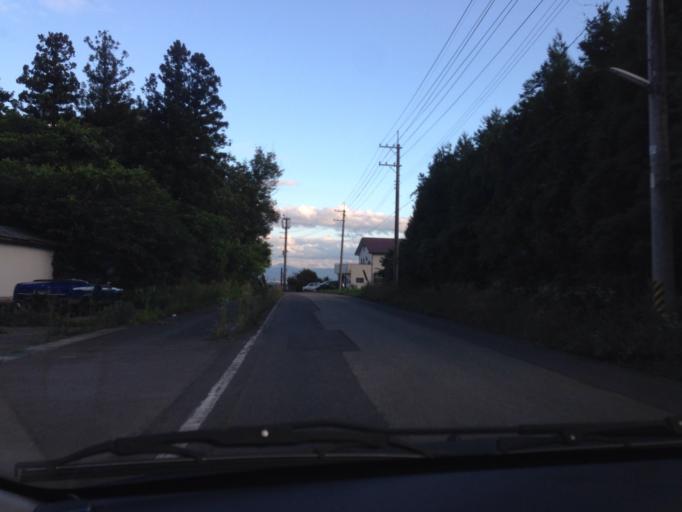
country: JP
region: Fukushima
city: Kitakata
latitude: 37.6900
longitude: 139.8578
